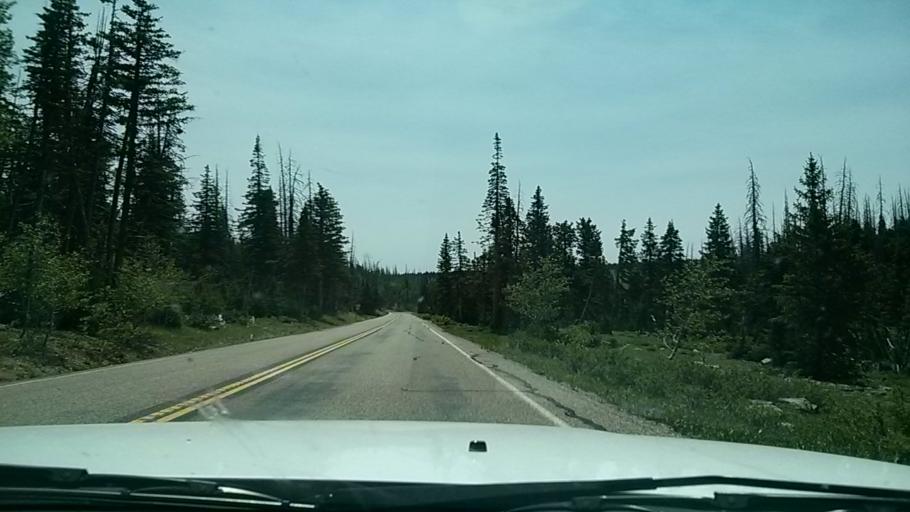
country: US
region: Utah
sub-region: Iron County
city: Cedar City
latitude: 37.5838
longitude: -112.8464
